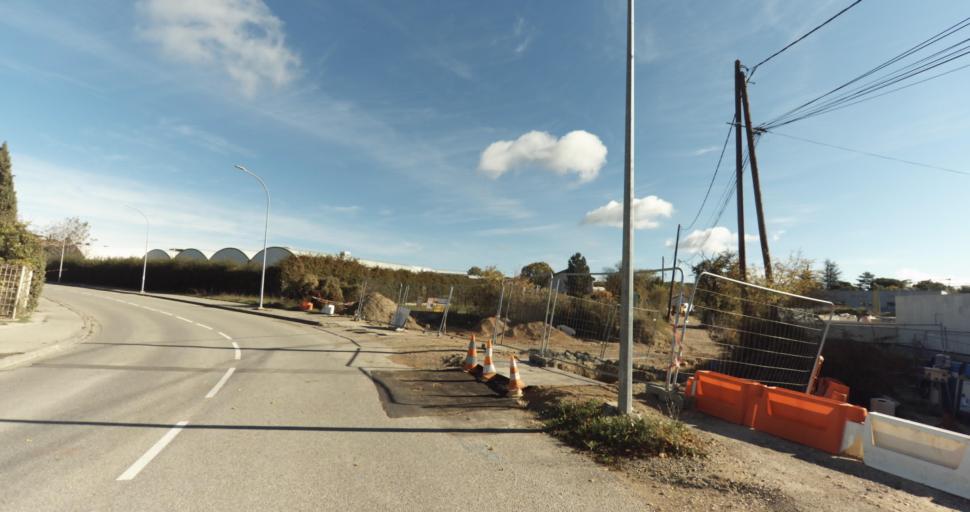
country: FR
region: Provence-Alpes-Cote d'Azur
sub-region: Departement des Bouches-du-Rhone
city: Venelles
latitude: 43.5903
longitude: 5.4765
